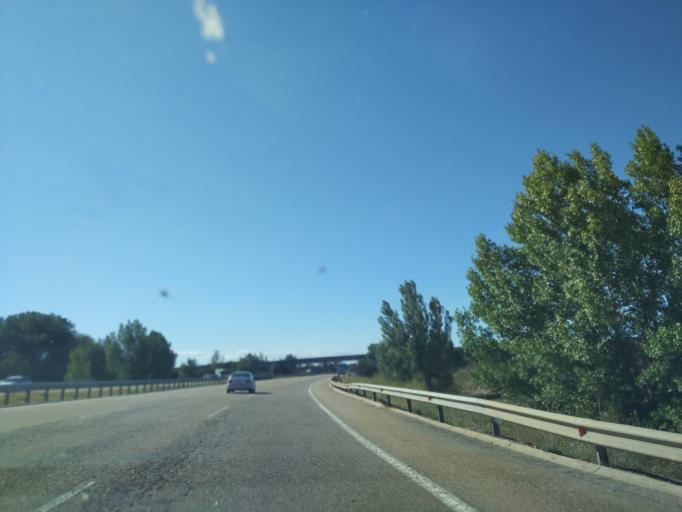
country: ES
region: Castille and Leon
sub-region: Provincia de Zamora
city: Villanueva de Azoague
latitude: 41.9877
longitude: -5.6345
